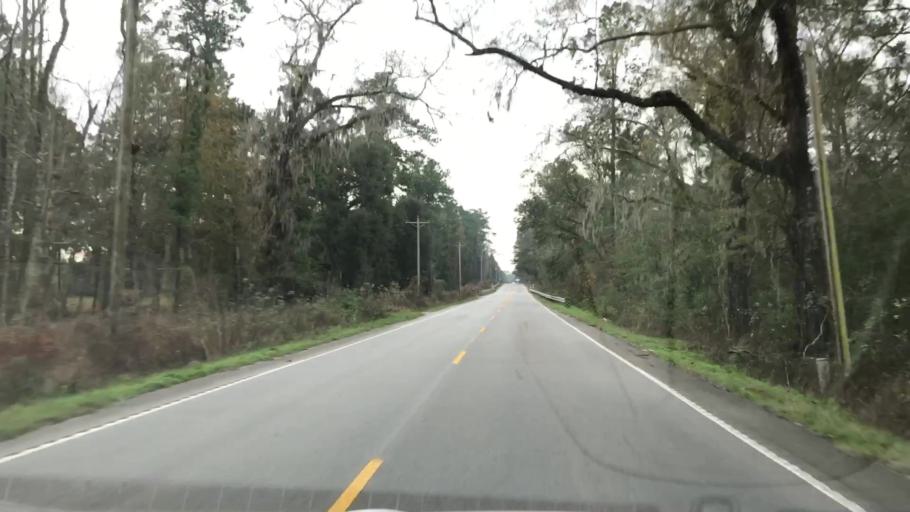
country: US
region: South Carolina
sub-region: Jasper County
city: Ridgeland
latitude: 32.5097
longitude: -80.8882
